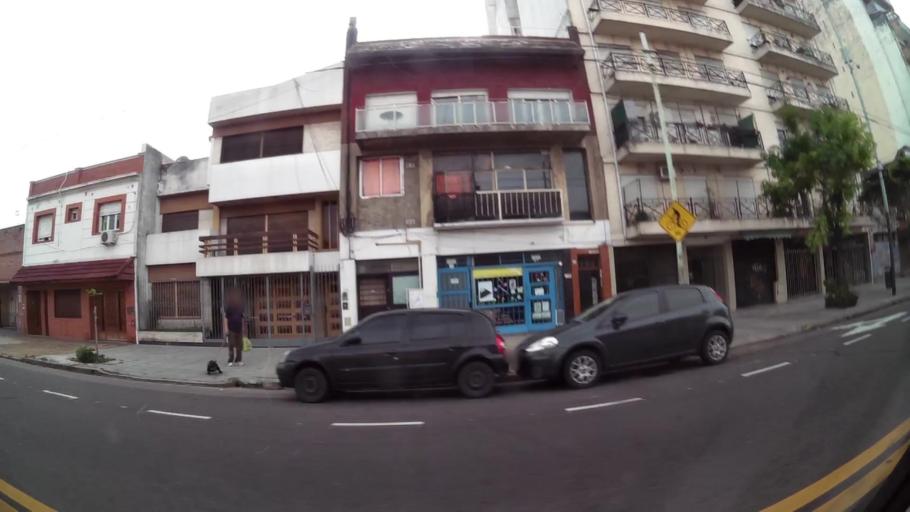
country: AR
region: Buenos Aires F.D.
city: Villa Santa Rita
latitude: -34.6389
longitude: -58.4318
